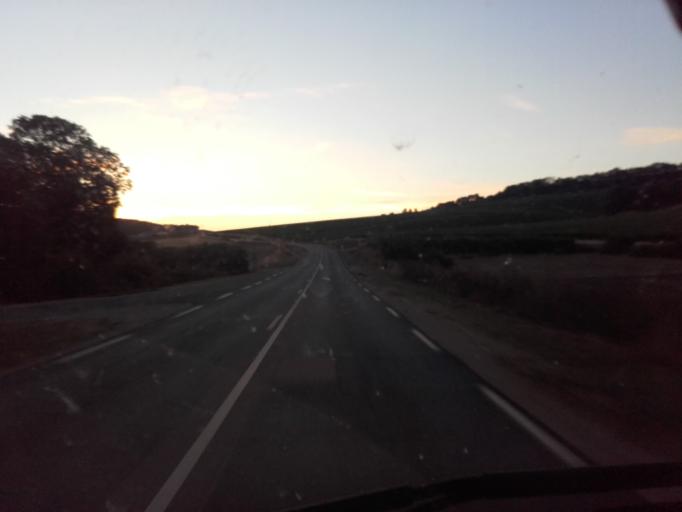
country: FR
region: Bourgogne
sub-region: Departement de l'Yonne
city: Chablis
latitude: 47.8116
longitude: 3.8451
